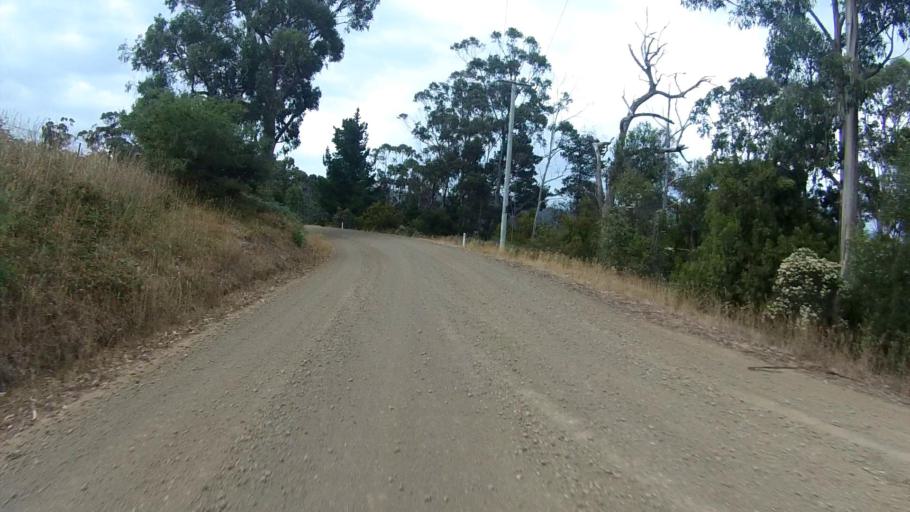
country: AU
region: Tasmania
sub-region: Huon Valley
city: Cygnet
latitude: -43.2357
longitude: 147.0989
